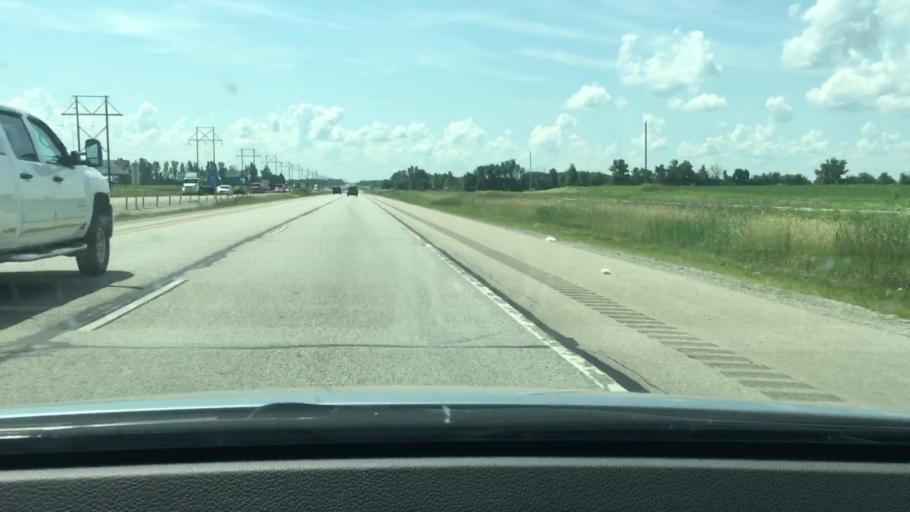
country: US
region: Wisconsin
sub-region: Winnebago County
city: Oshkosh
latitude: 43.9360
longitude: -88.5835
